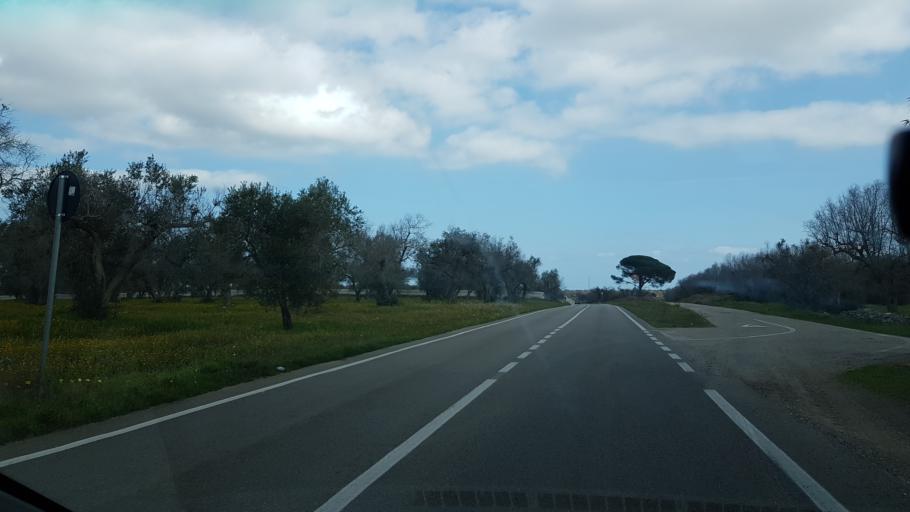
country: IT
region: Apulia
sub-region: Provincia di Brindisi
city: Torchiarolo
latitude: 40.4609
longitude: 18.0701
